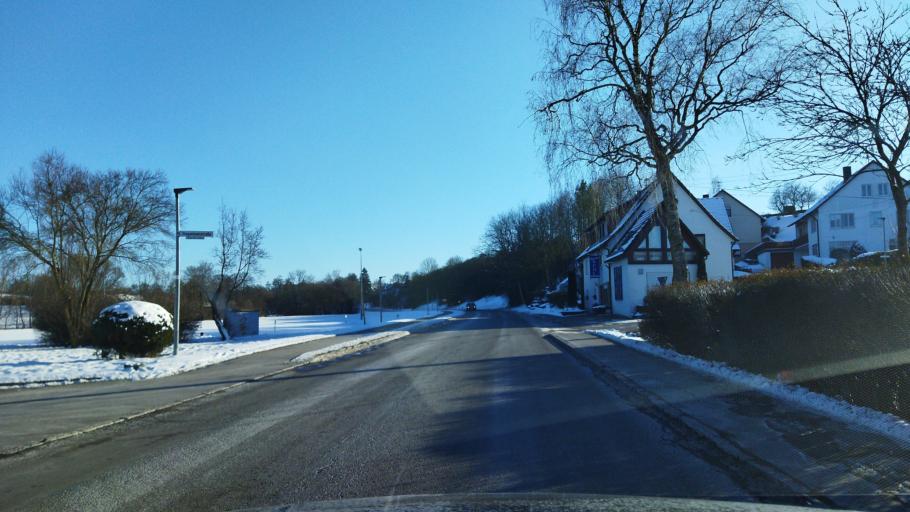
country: DE
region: Baden-Wuerttemberg
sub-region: Regierungsbezirk Stuttgart
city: Obersontheim
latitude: 49.0648
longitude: 9.8923
